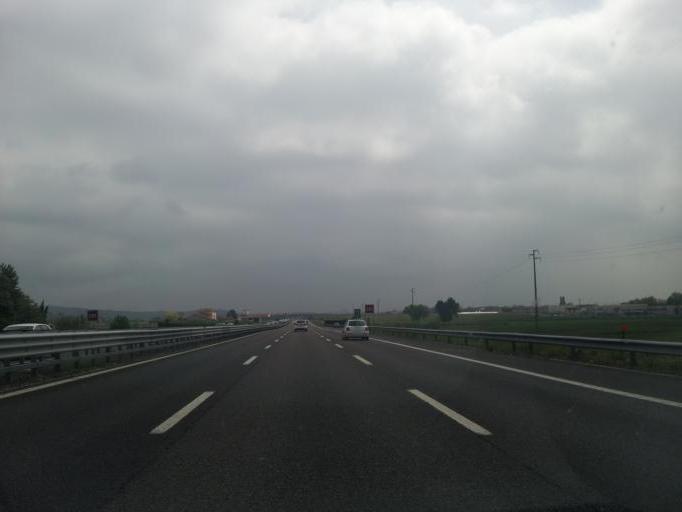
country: IT
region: Veneto
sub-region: Provincia di Verona
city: Caldiero
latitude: 45.4140
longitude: 11.2025
